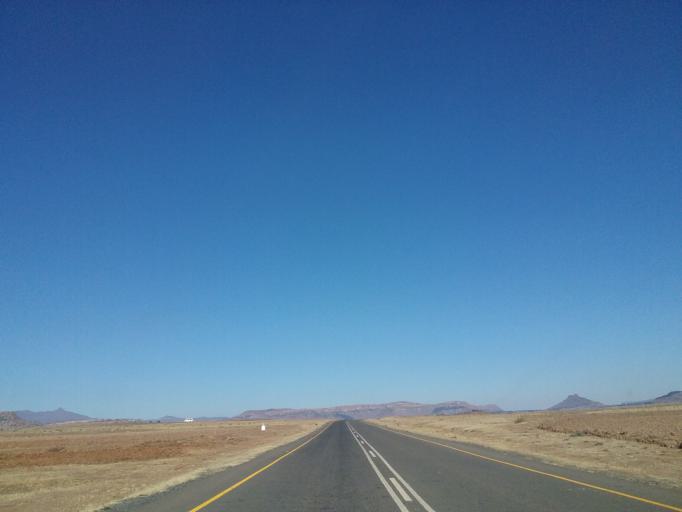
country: LS
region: Maseru
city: Maseru
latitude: -29.4370
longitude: 27.6463
